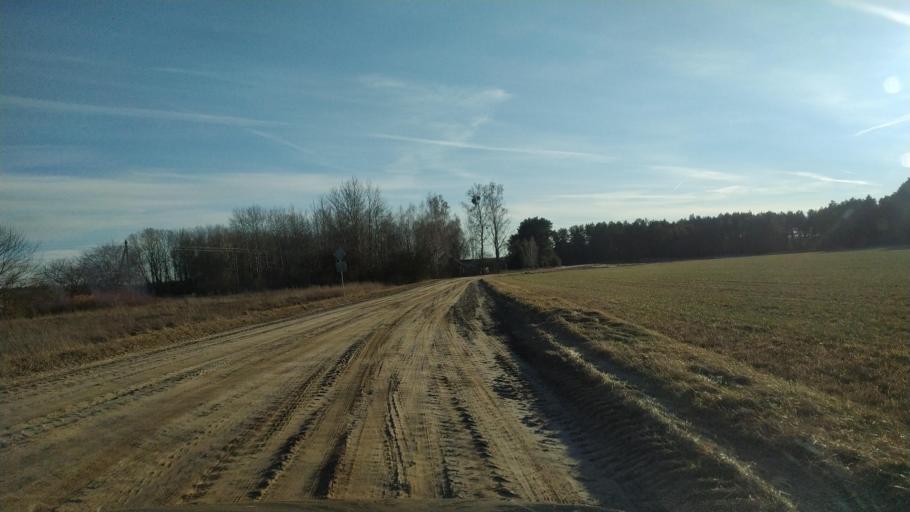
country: BY
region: Brest
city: Pruzhany
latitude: 52.5517
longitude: 24.2876
